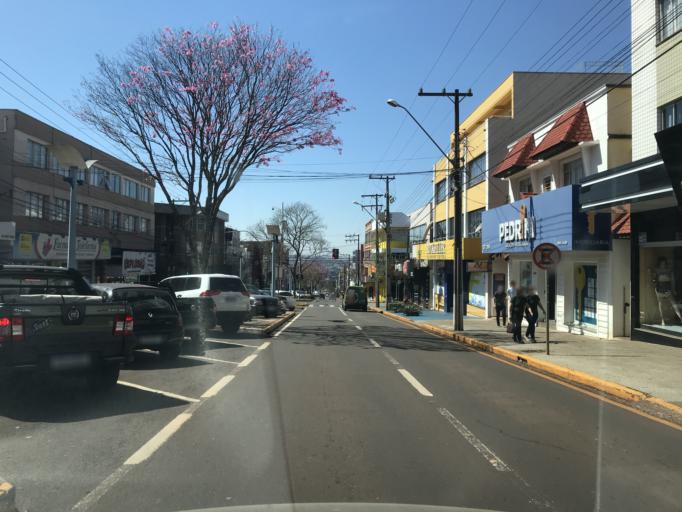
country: BR
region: Parana
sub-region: Toledo
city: Toledo
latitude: -24.7343
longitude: -53.7415
